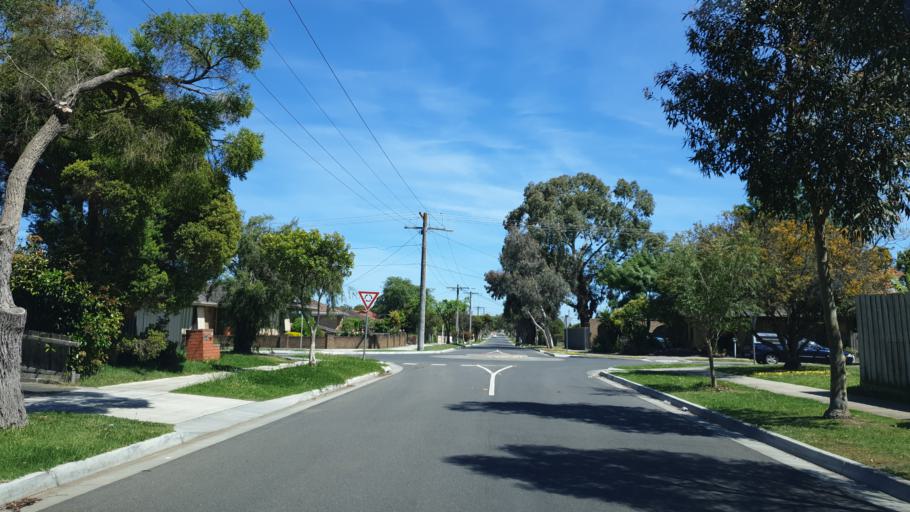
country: AU
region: Victoria
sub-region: Casey
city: Cranbourne
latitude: -38.1067
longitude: 145.2772
